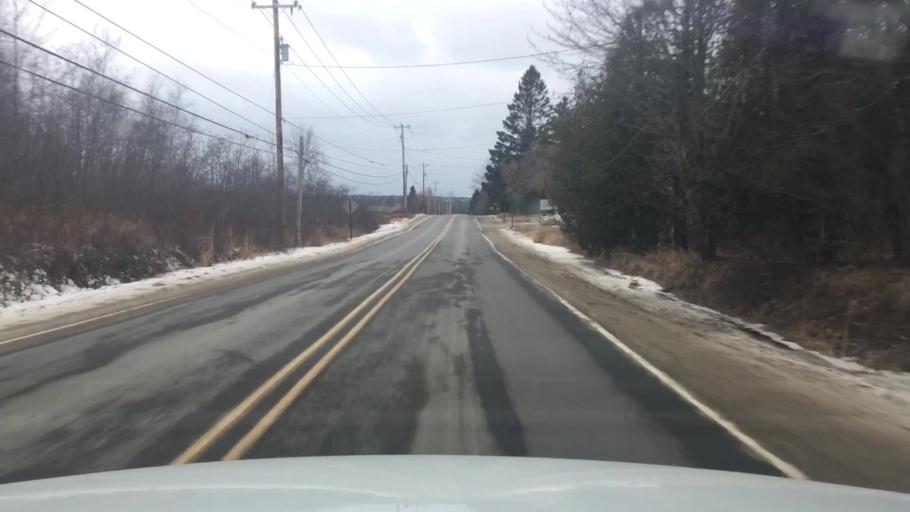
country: US
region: Maine
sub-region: Washington County
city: Addison
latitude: 44.6210
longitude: -67.7046
